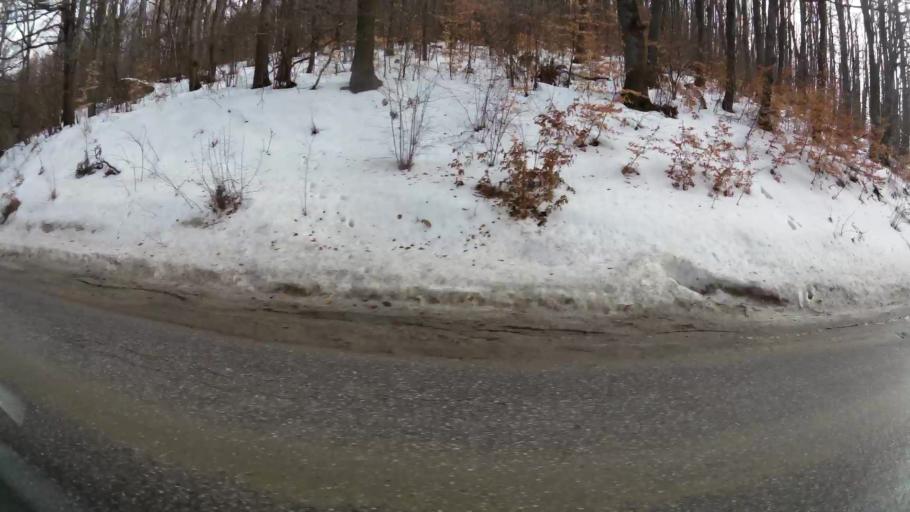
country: BG
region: Sofia-Capital
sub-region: Stolichna Obshtina
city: Sofia
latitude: 42.6349
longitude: 23.2254
